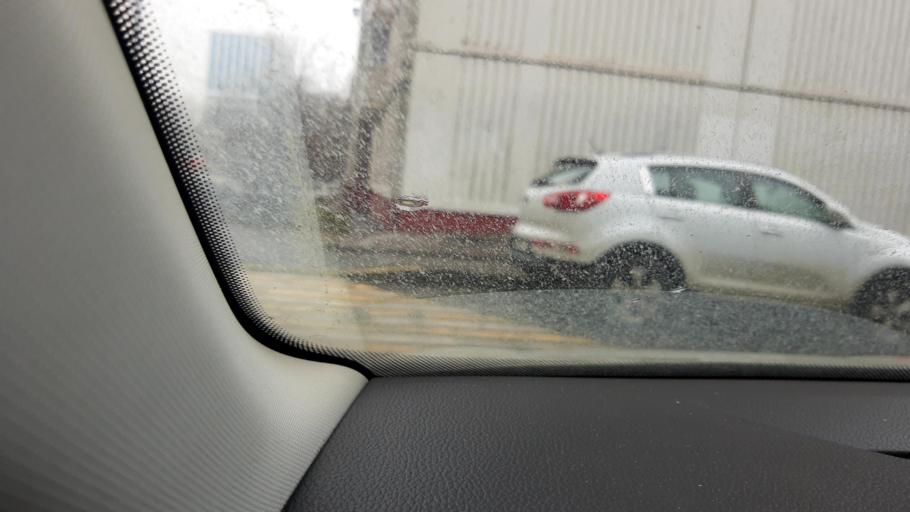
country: RU
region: Moskovskaya
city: Kur'yanovo
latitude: 55.6408
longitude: 37.6939
